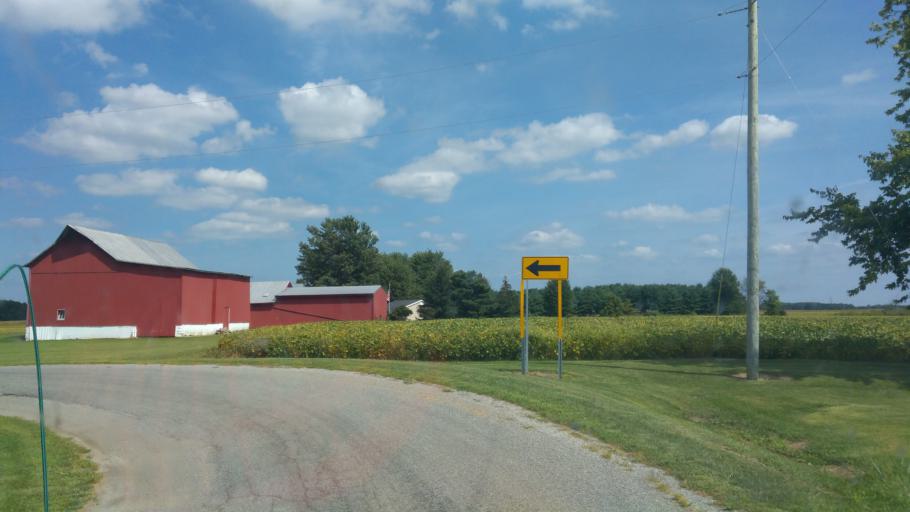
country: US
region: Ohio
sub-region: Union County
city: Richwood
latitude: 40.3972
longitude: -83.4445
